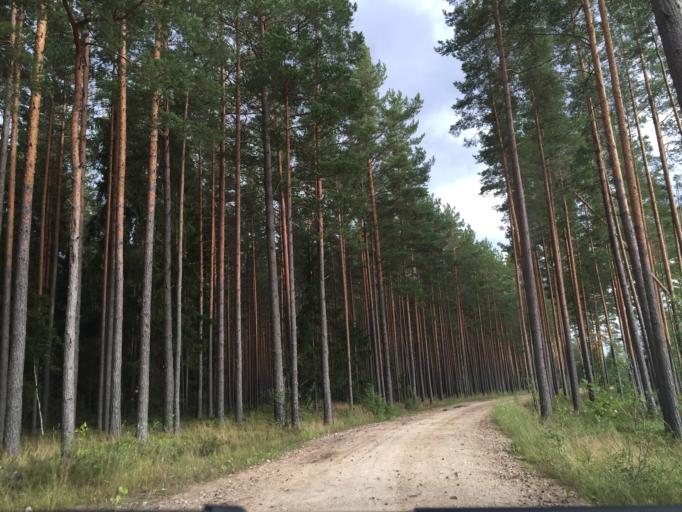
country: LV
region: Saulkrastu
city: Saulkrasti
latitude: 57.2174
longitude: 24.4198
